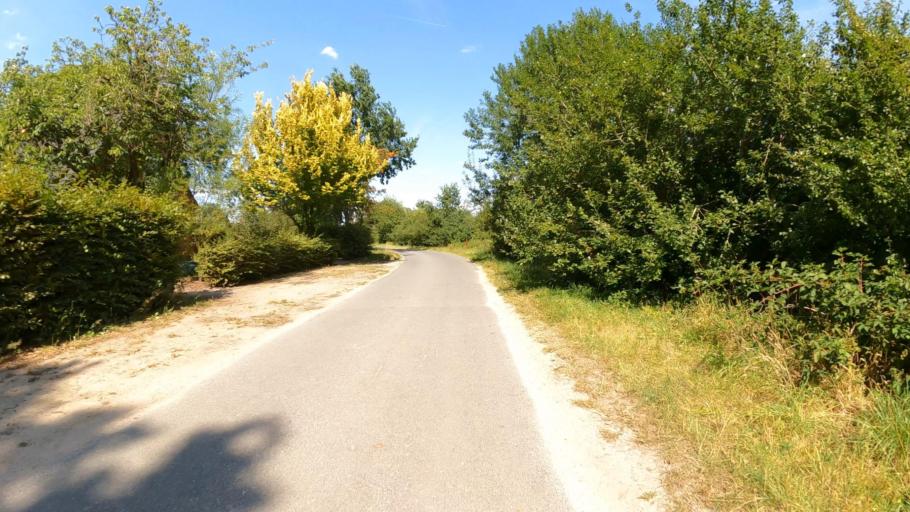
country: DE
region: Schleswig-Holstein
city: Ellerhoop
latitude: 53.7203
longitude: 9.7784
